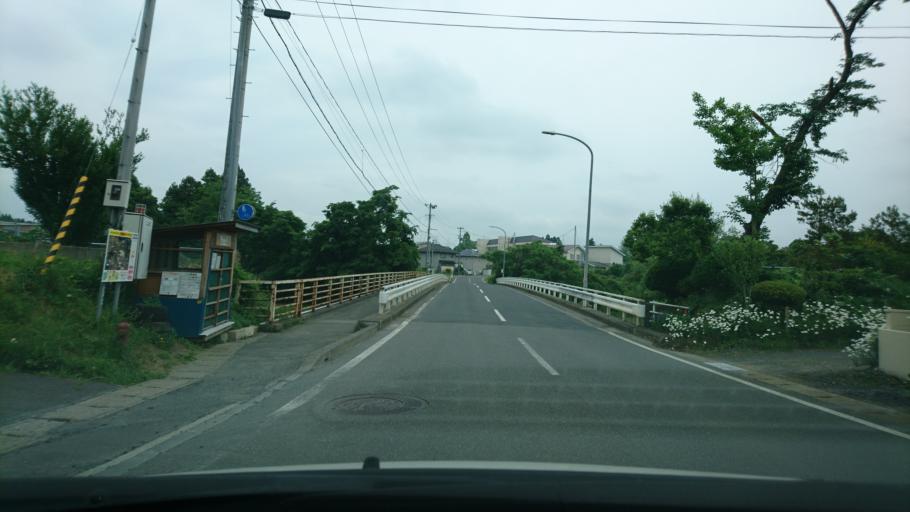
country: JP
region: Iwate
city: Ichinoseki
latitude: 38.9231
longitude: 141.0902
